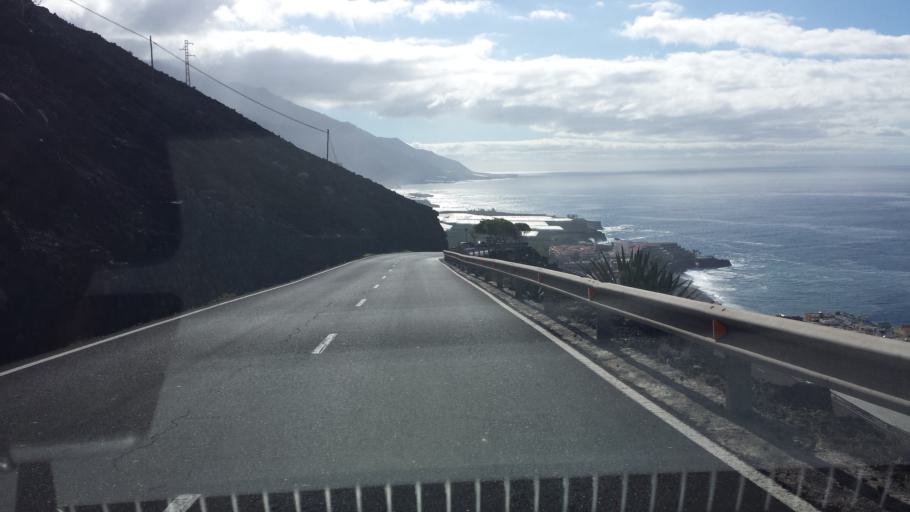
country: ES
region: Canary Islands
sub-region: Provincia de Santa Cruz de Tenerife
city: Tazacorte
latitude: 28.5937
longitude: -17.9113
